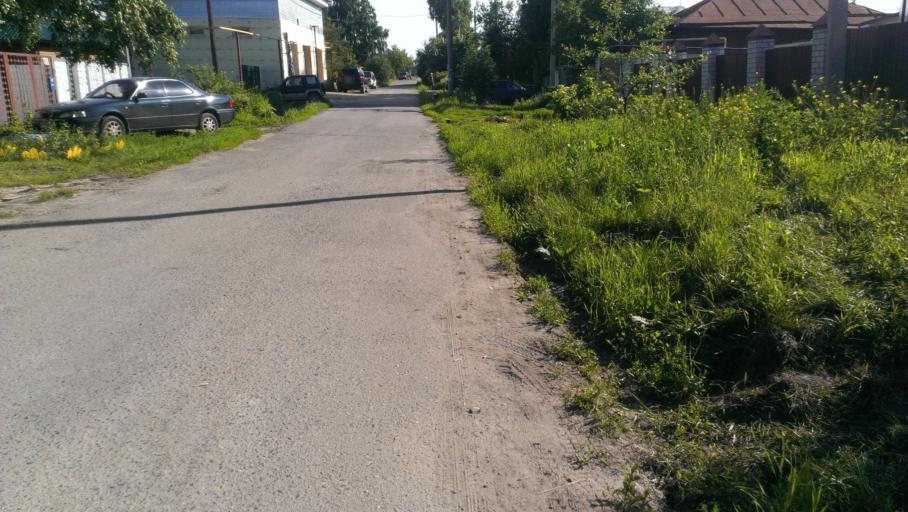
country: RU
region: Altai Krai
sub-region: Gorod Barnaulskiy
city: Barnaul
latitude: 53.3564
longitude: 83.7405
